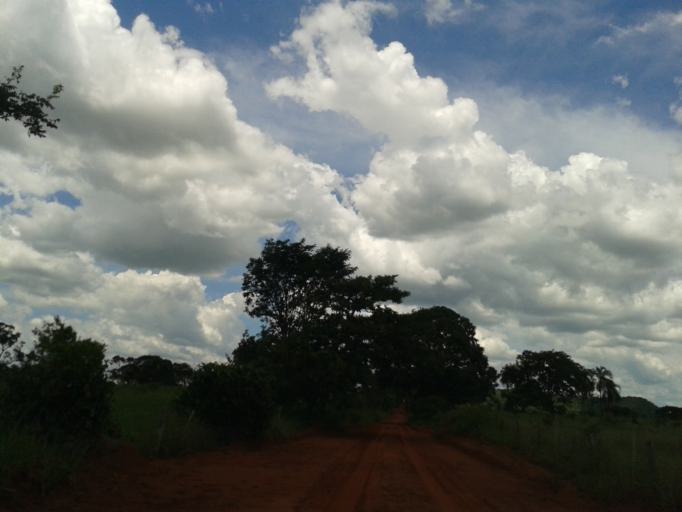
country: BR
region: Minas Gerais
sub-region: Ituiutaba
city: Ituiutaba
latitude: -18.8477
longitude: -49.5120
